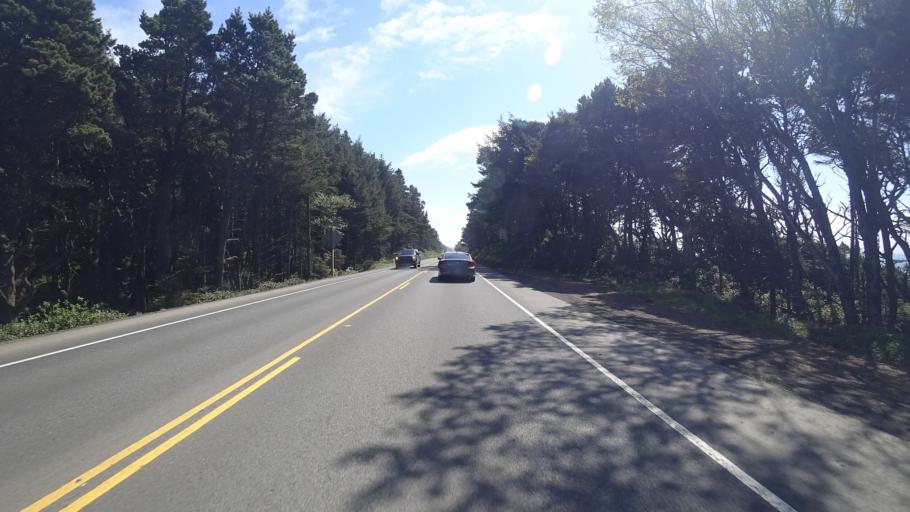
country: US
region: Oregon
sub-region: Lincoln County
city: Depoe Bay
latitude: 44.7375
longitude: -124.0564
